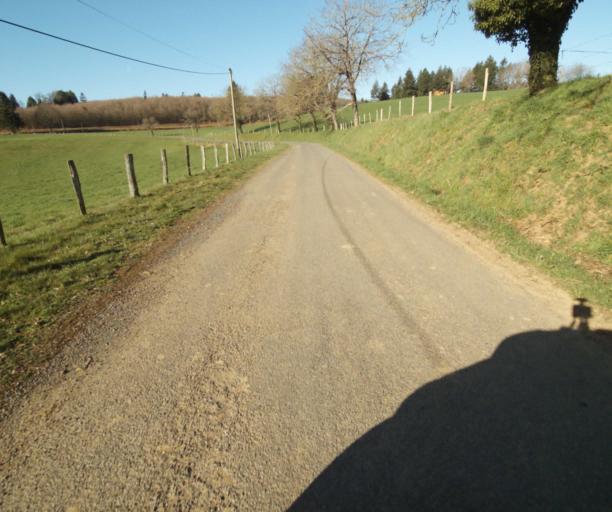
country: FR
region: Limousin
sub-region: Departement de la Correze
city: Seilhac
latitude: 45.3559
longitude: 1.7479
